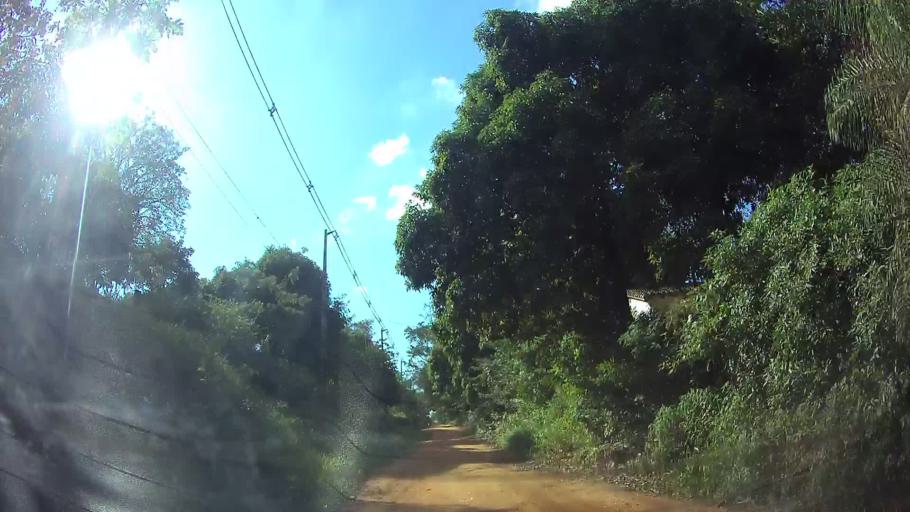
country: PY
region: Central
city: Limpio
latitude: -25.2512
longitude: -57.4748
